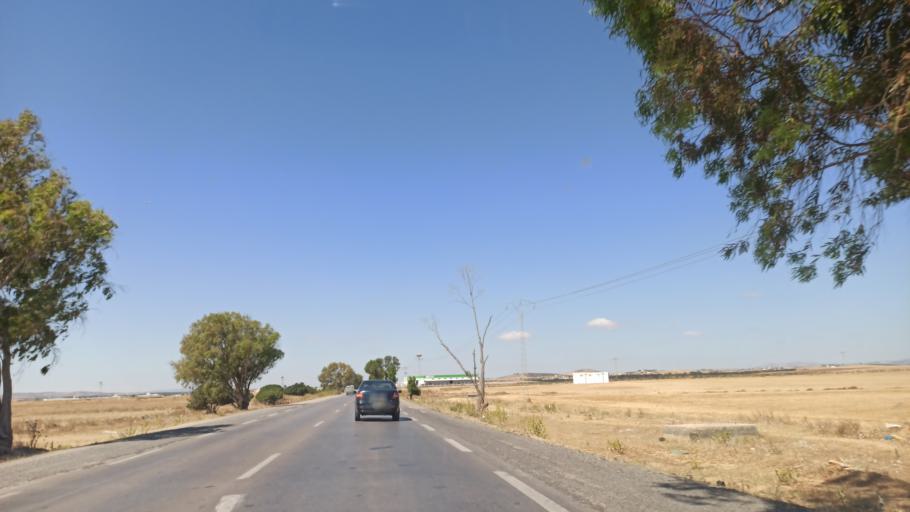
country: TN
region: Tunis
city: Oued Lill
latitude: 36.7424
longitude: 9.9581
